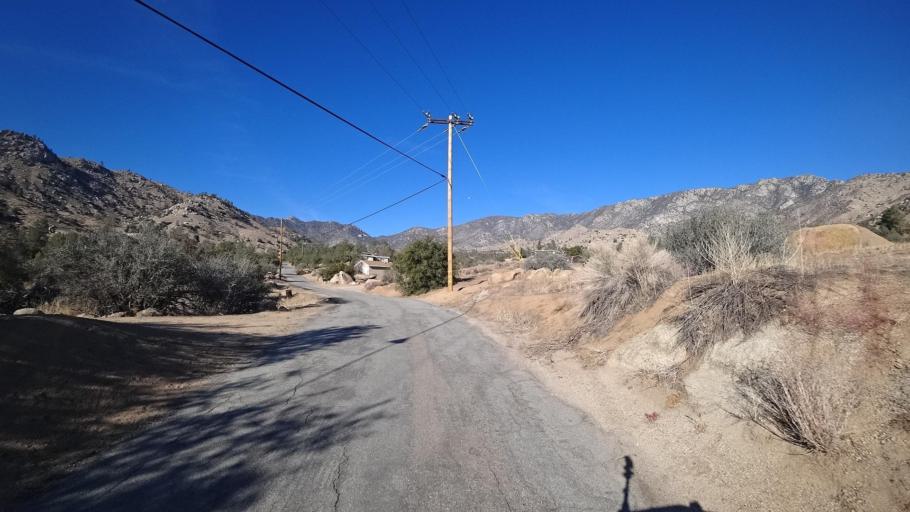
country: US
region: California
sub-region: Kern County
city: Weldon
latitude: 35.7128
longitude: -118.3049
